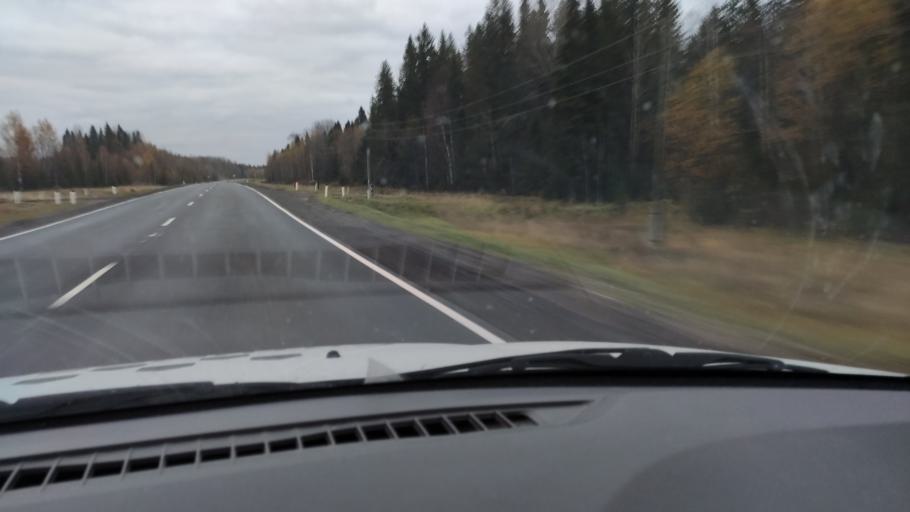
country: RU
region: Kirov
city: Lesnyye Polyany
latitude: 58.8299
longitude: 52.6422
